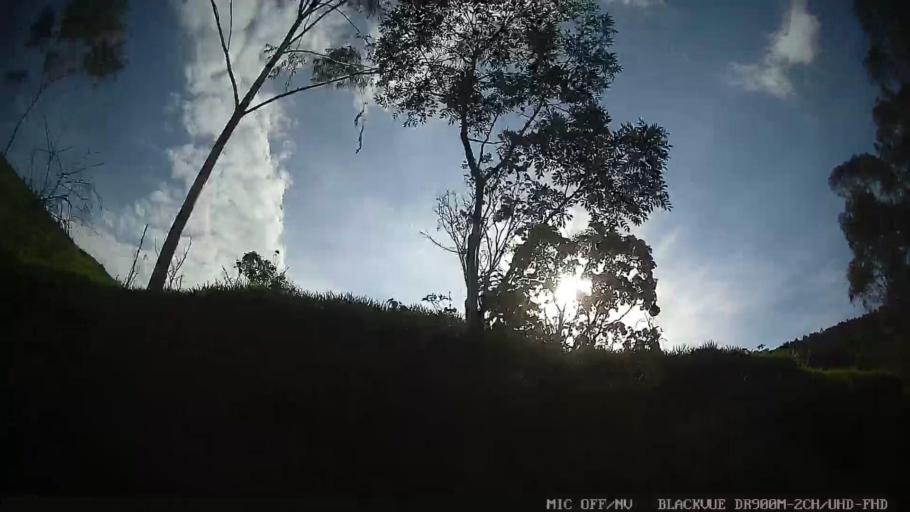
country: BR
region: Sao Paulo
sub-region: Serra Negra
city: Serra Negra
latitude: -22.6660
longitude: -46.6878
